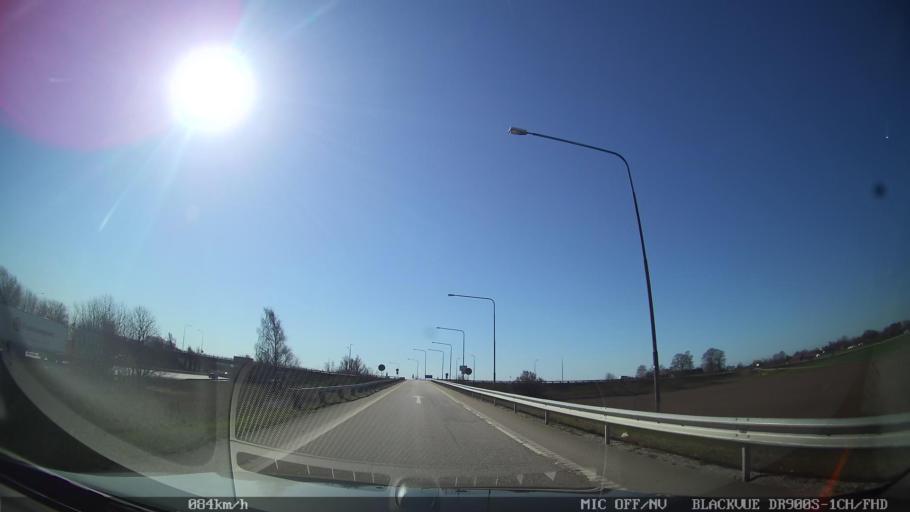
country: SE
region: Skane
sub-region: Malmo
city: Tygelsjo
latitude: 55.5318
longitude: 13.0066
